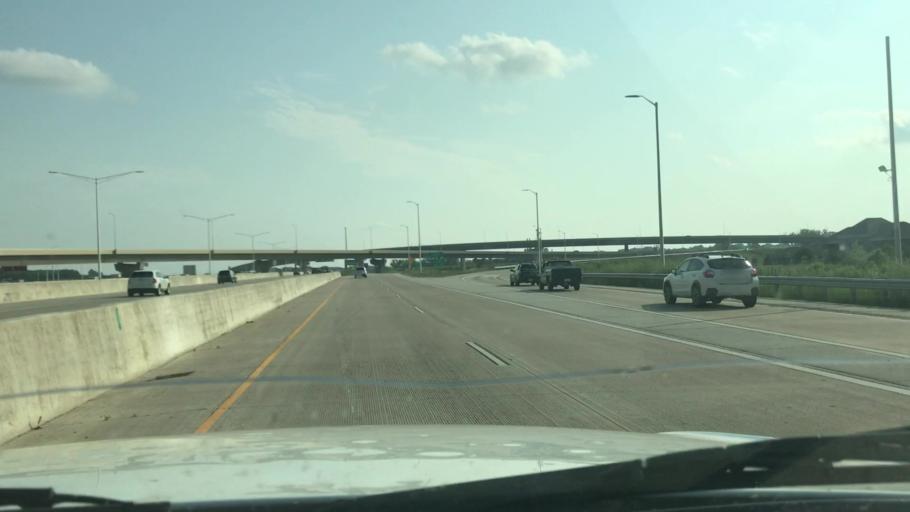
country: US
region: Wisconsin
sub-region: Brown County
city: Howard
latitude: 44.5425
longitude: -88.0742
